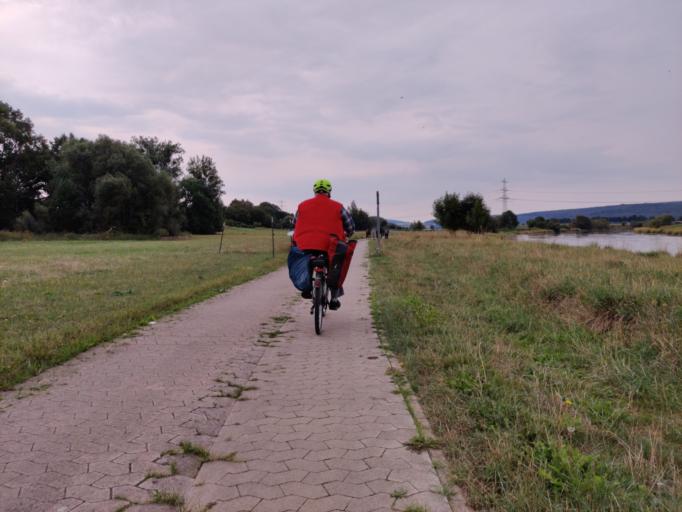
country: DE
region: Lower Saxony
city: Hehlen
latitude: 52.0307
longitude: 9.4299
